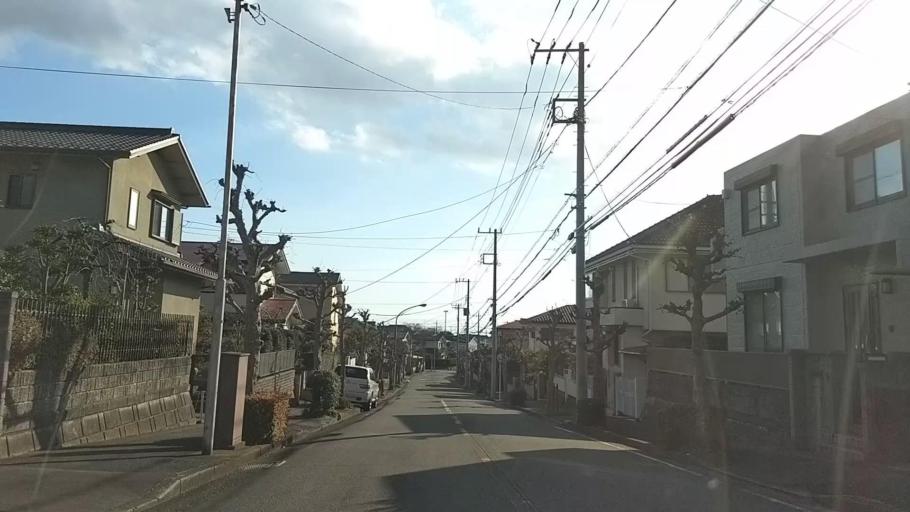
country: JP
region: Kanagawa
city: Atsugi
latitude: 35.4384
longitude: 139.3283
